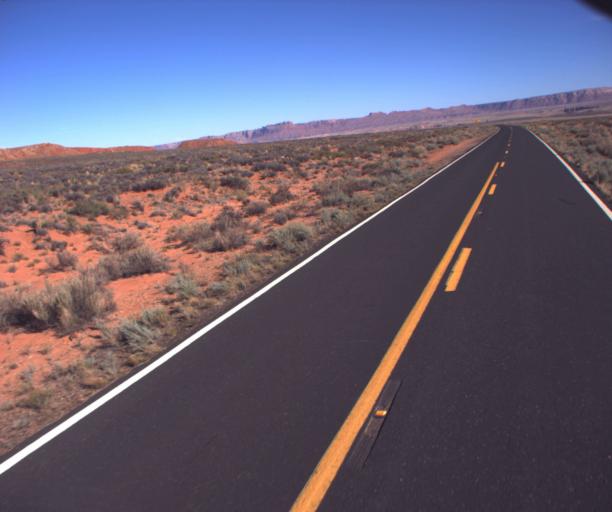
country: US
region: Arizona
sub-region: Coconino County
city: Page
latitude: 36.6847
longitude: -111.8582
